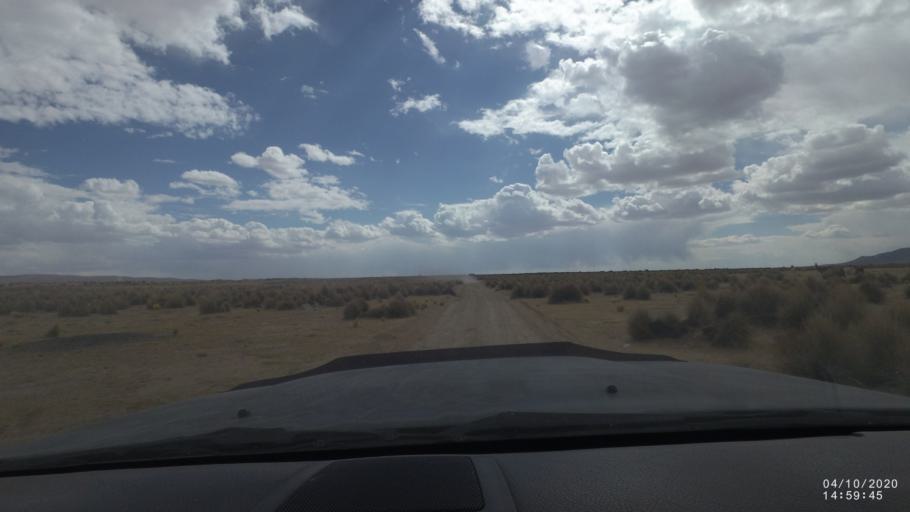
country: BO
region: Oruro
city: Poopo
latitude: -18.6862
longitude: -67.5241
